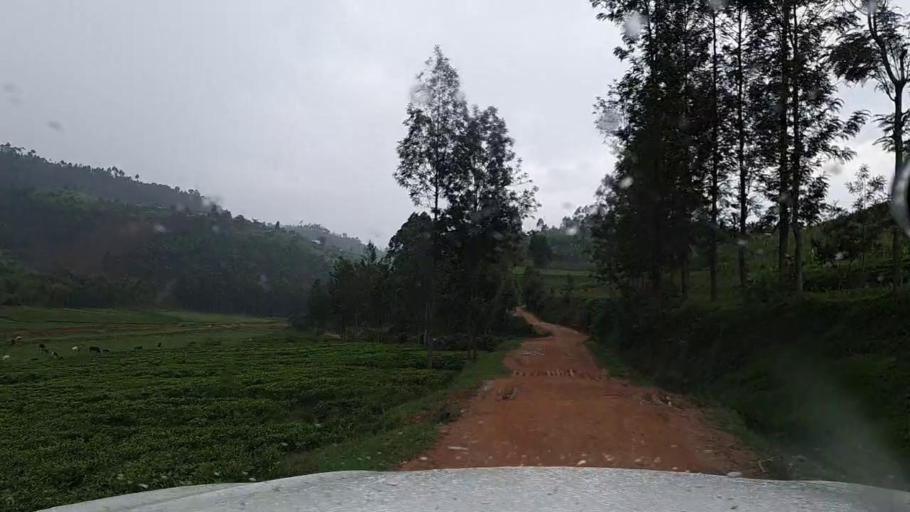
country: RW
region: Northern Province
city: Byumba
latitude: -1.6515
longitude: 29.9282
